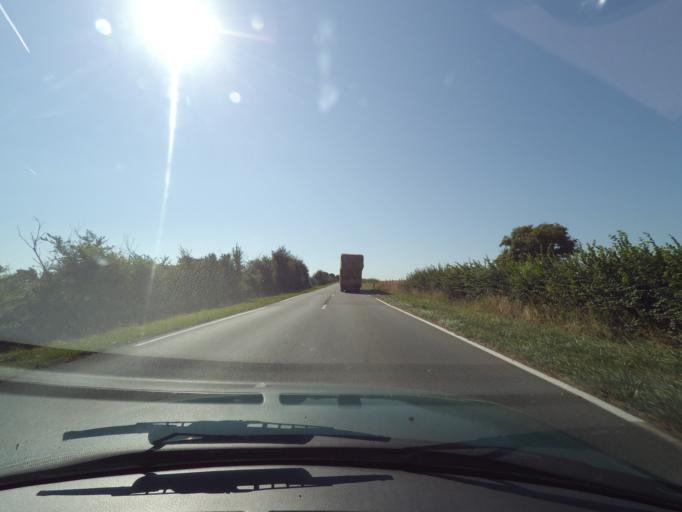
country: FR
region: Poitou-Charentes
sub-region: Departement de la Vienne
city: Lussac-les-Chateaux
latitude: 46.3831
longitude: 0.7483
